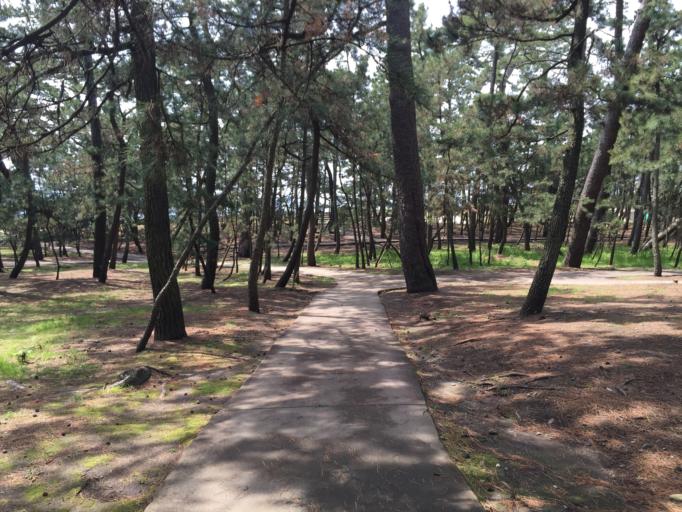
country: JP
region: Shizuoka
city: Numazu
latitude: 35.0697
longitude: 138.8748
